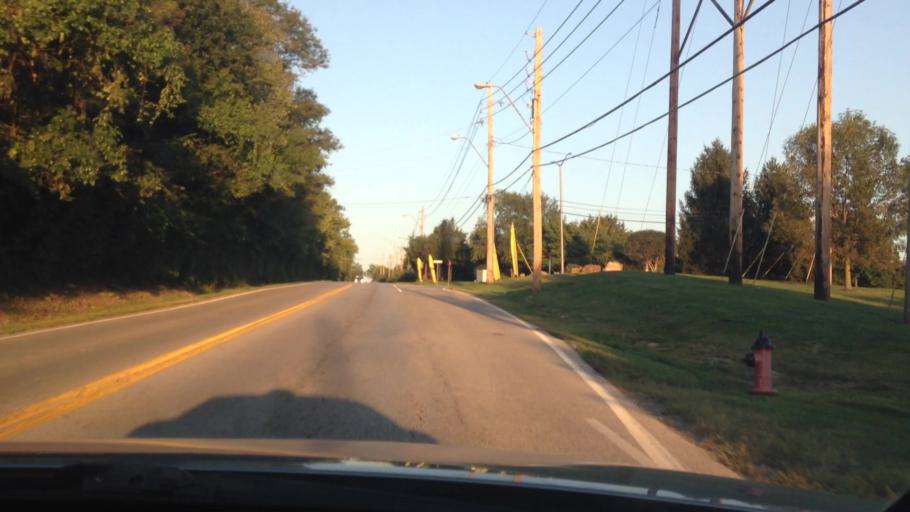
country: US
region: Missouri
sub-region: Jackson County
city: Grandview
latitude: 38.9249
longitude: -94.5603
